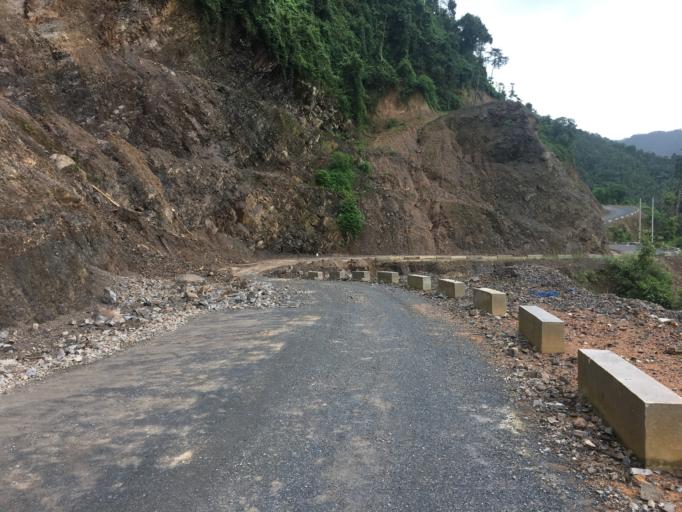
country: VN
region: Ha Giang
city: Thi Tran Tam Son
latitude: 22.9632
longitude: 105.0404
